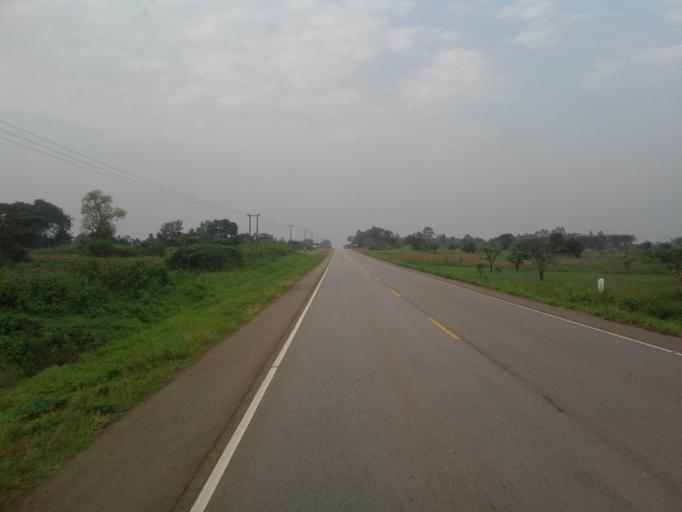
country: UG
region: Eastern Region
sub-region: Tororo District
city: Tororo
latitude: 0.6135
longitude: 34.0822
